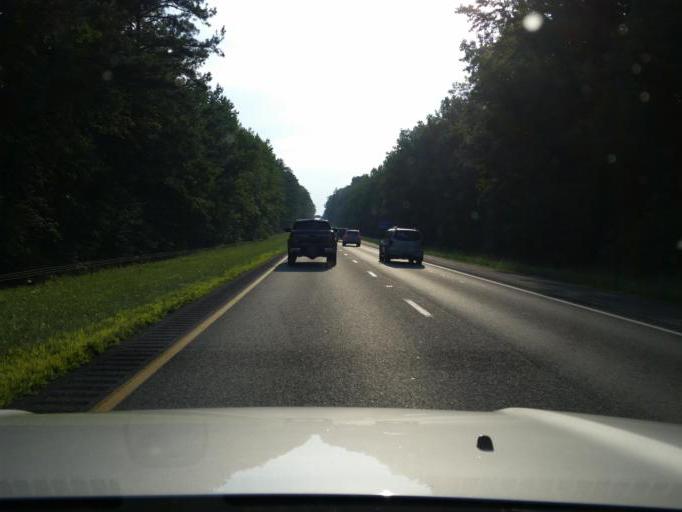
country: US
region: Virginia
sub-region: Henrico County
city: Sandston
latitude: 37.5109
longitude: -77.1481
